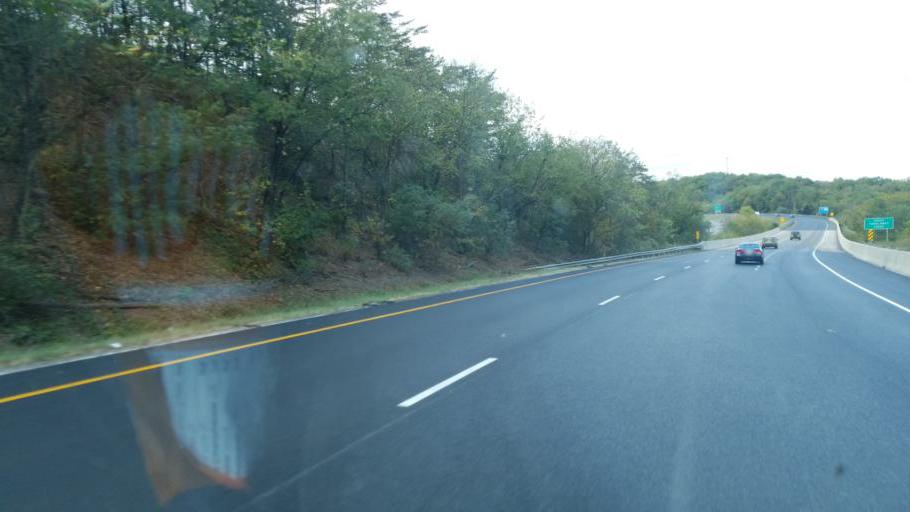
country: US
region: Maryland
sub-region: Washington County
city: Hancock
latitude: 39.6974
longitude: -78.1526
